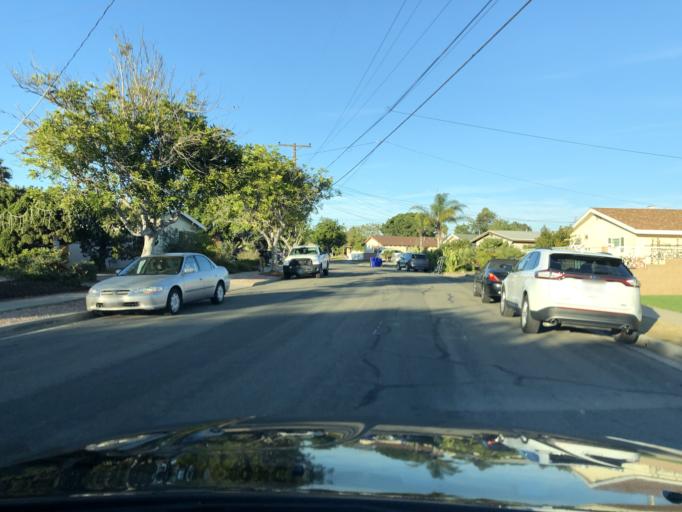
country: US
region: California
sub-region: San Diego County
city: La Jolla
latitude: 32.8155
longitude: -117.1952
